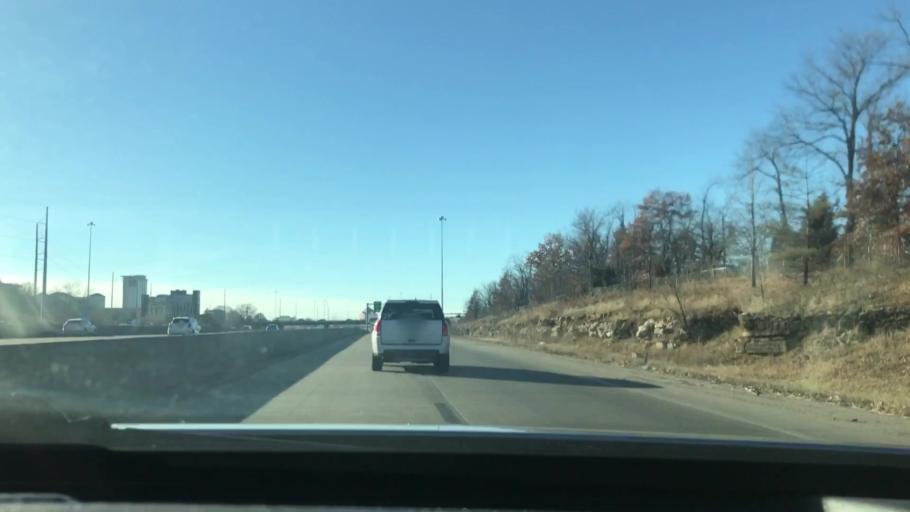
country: US
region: Kansas
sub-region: Johnson County
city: Leawood
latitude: 38.9312
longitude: -94.6470
